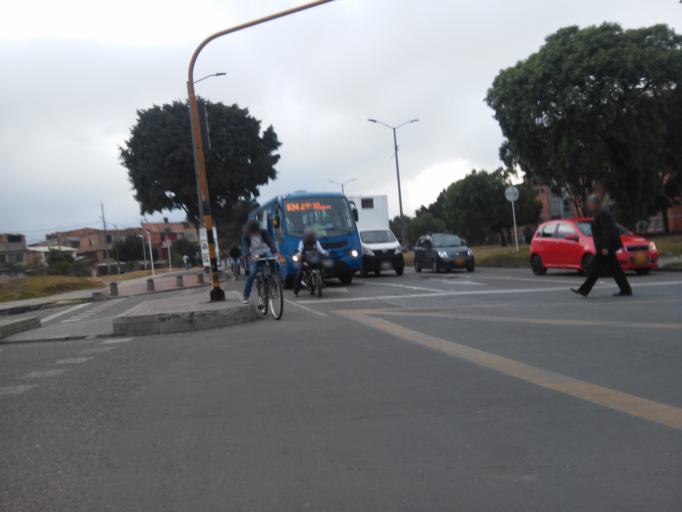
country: CO
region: Cundinamarca
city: Soacha
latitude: 4.6133
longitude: -74.1718
